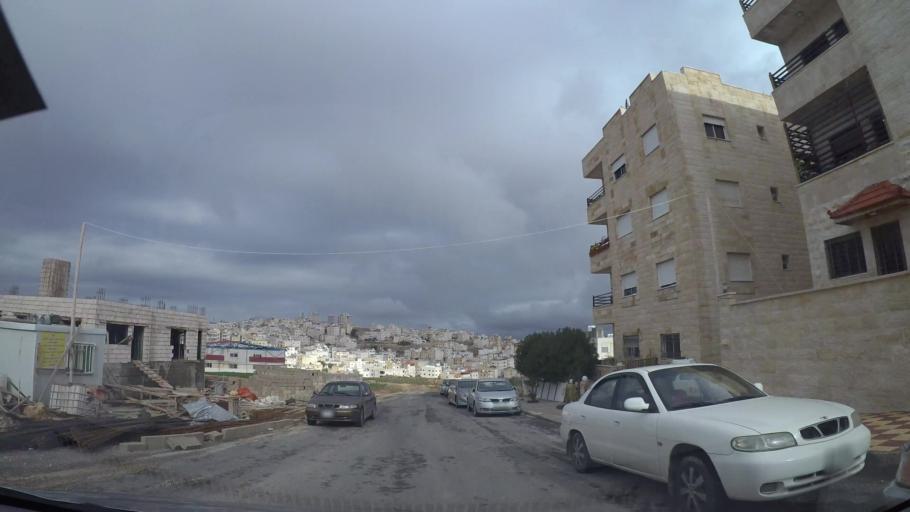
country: JO
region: Amman
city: Al Jubayhah
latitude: 32.0620
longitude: 35.8876
